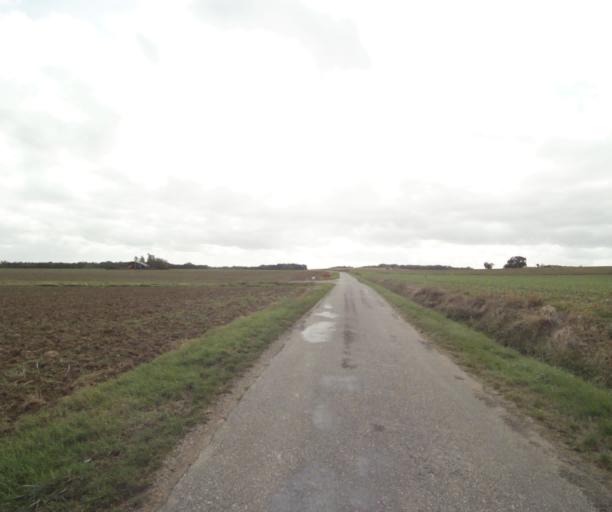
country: FR
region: Midi-Pyrenees
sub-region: Departement du Tarn-et-Garonne
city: Beaumont-de-Lomagne
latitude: 43.8735
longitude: 1.0889
